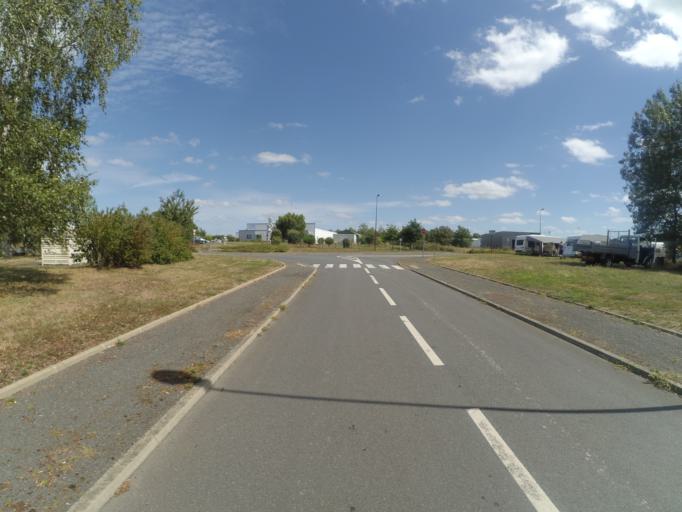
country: FR
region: Pays de la Loire
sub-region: Departement de la Loire-Atlantique
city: Clisson
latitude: 47.0775
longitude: -1.2906
